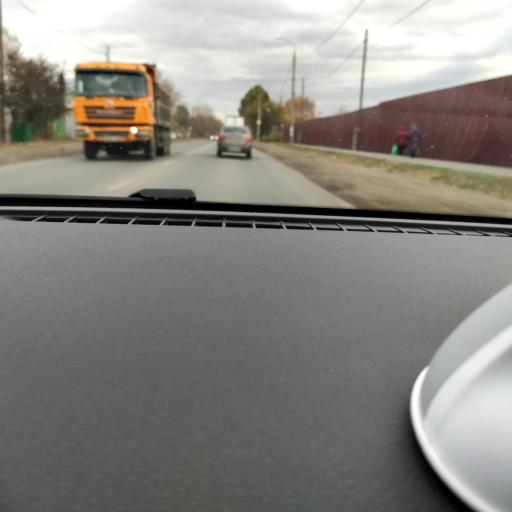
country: RU
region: Samara
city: Petra-Dubrava
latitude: 53.2521
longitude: 50.3416
